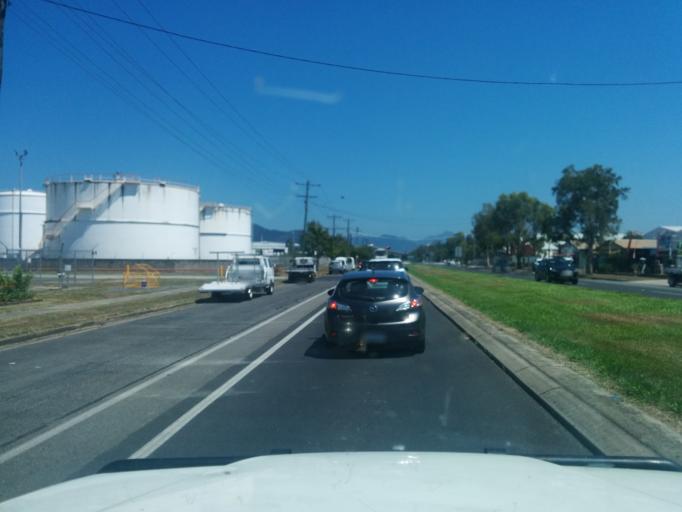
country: AU
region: Queensland
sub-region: Cairns
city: Cairns
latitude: -16.9334
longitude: 145.7745
